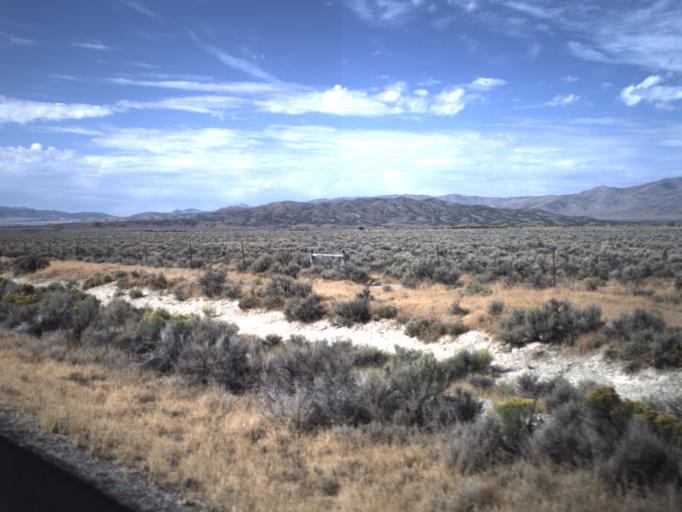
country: US
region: Idaho
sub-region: Cassia County
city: Burley
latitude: 41.7001
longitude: -113.5338
